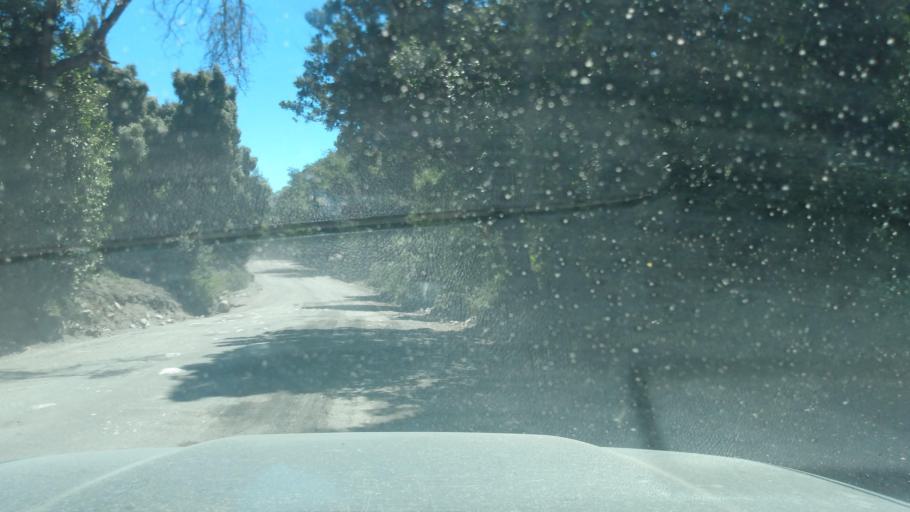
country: AR
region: Neuquen
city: Villa La Angostura
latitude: -40.6283
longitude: -71.4878
